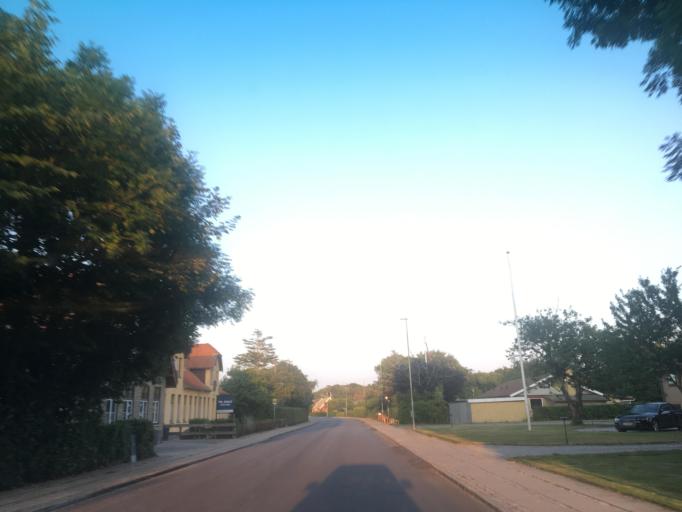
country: DK
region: North Denmark
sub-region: Thisted Kommune
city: Hurup
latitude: 56.7644
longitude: 8.3083
